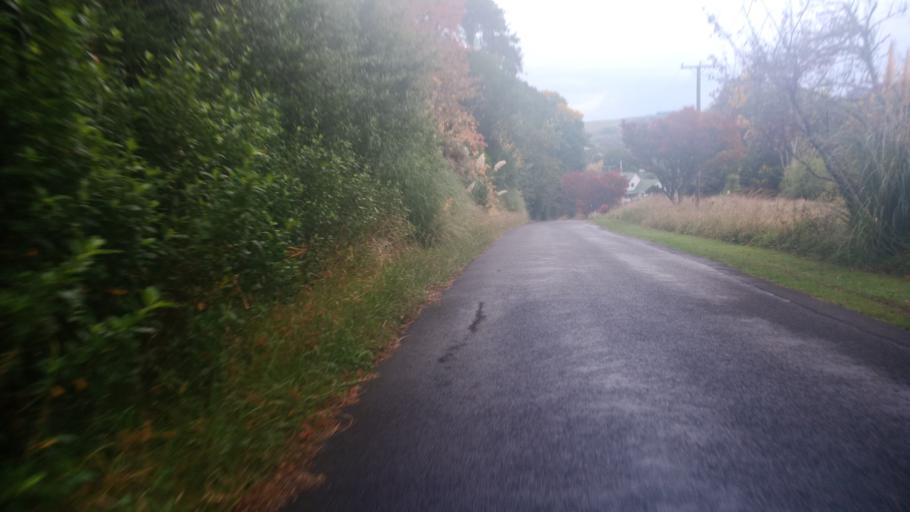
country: NZ
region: Gisborne
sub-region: Gisborne District
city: Gisborne
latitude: -38.6609
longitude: 178.0417
